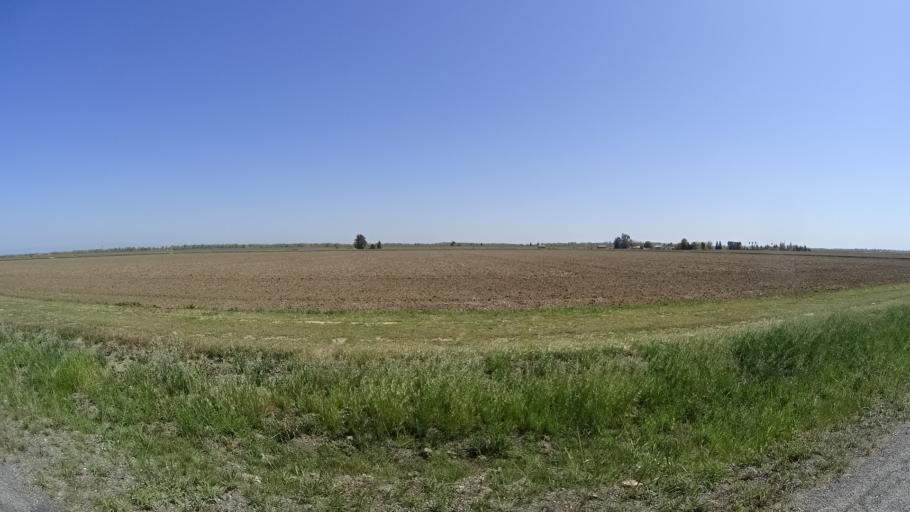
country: US
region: California
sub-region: Glenn County
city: Willows
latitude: 39.5701
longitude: -122.0278
